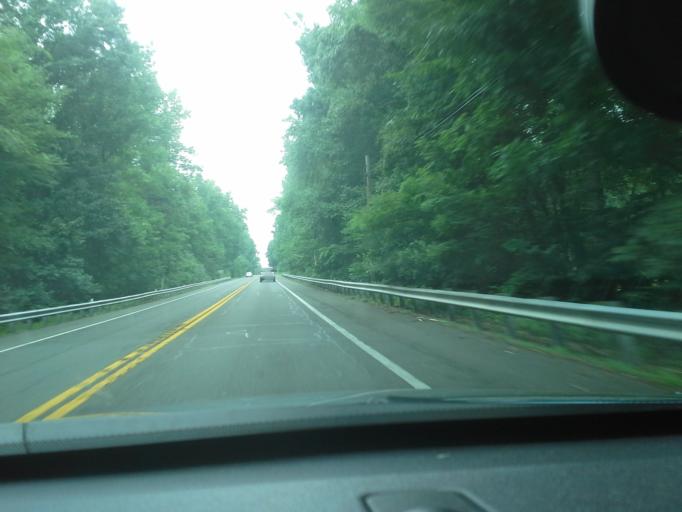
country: US
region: Maryland
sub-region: Calvert County
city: Owings
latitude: 38.7344
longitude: -76.6220
